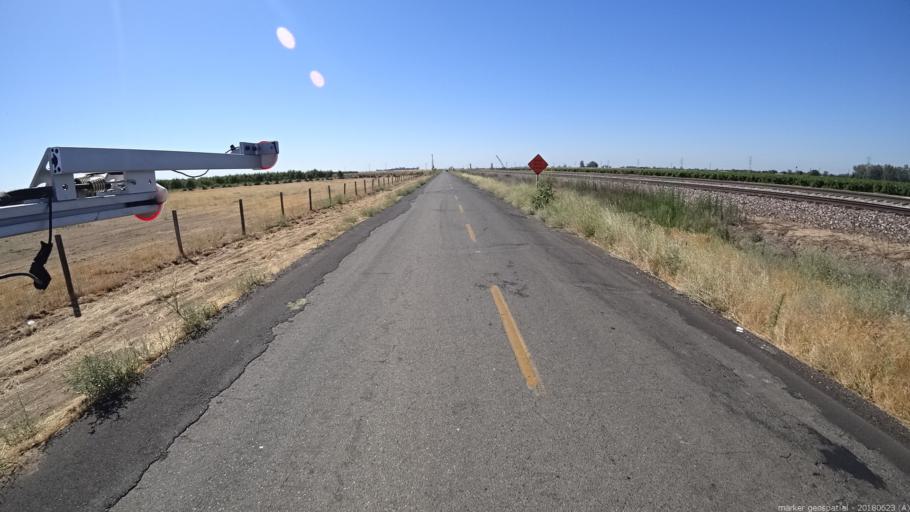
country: US
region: California
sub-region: Madera County
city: Parksdale
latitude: 36.9714
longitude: -120.0161
